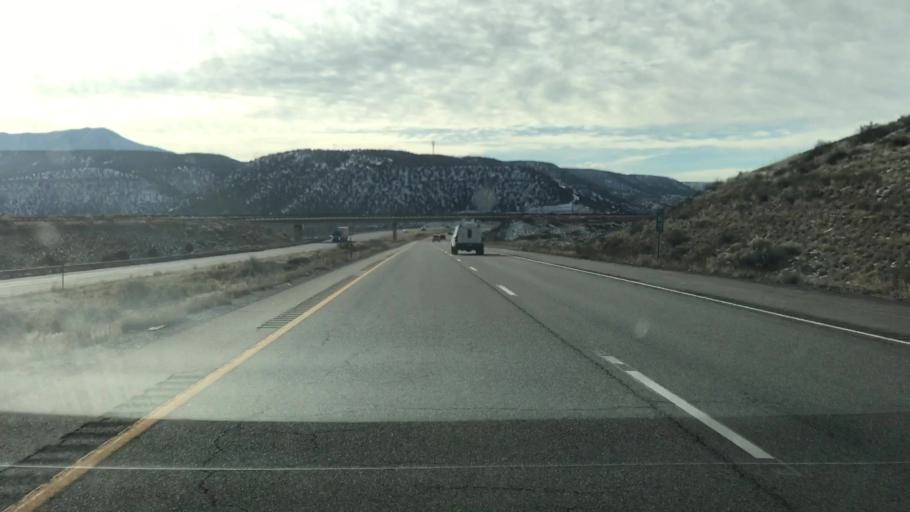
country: US
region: Colorado
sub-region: Garfield County
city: Parachute
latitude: 39.3606
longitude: -108.1705
